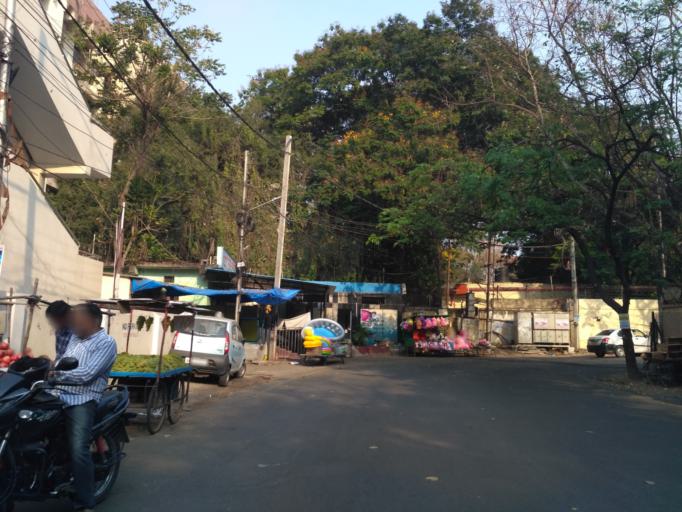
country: IN
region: Telangana
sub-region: Hyderabad
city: Hyderabad
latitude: 17.4086
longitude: 78.4682
